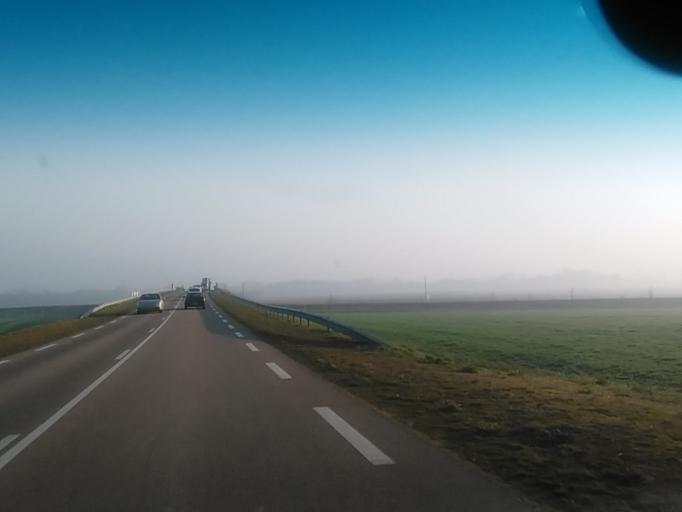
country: FR
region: Lower Normandy
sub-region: Departement du Calvados
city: Falaise
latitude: 48.8723
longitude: -0.2160
